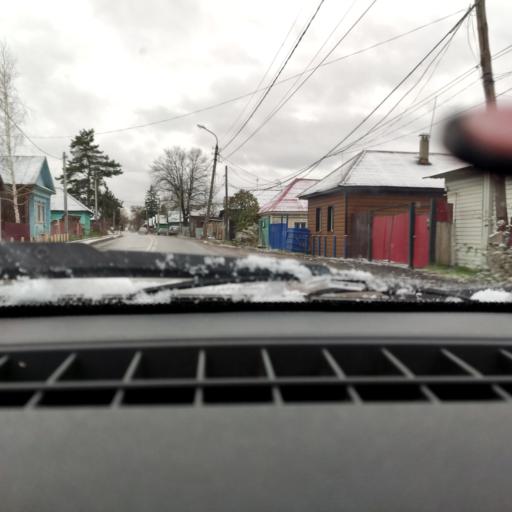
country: RU
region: Bashkortostan
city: Ufa
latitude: 54.8251
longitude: 56.1807
